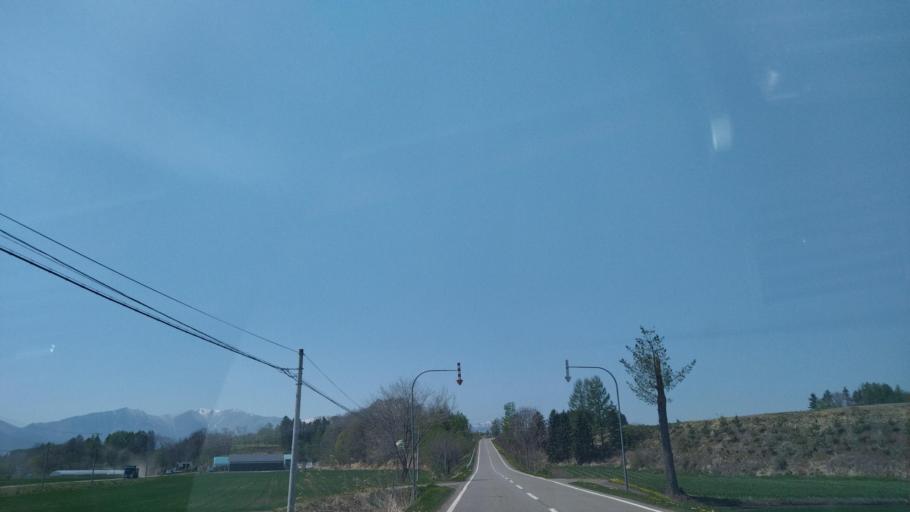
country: JP
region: Hokkaido
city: Obihiro
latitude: 42.9032
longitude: 143.0083
